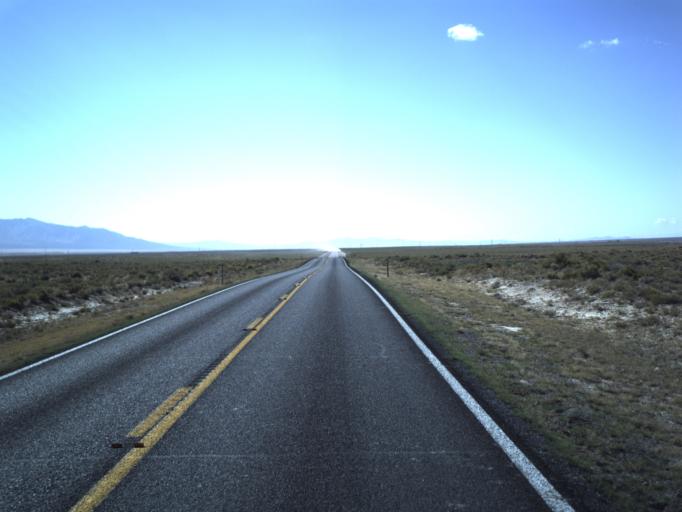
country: US
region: Utah
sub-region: Beaver County
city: Milford
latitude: 38.5305
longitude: -112.9912
